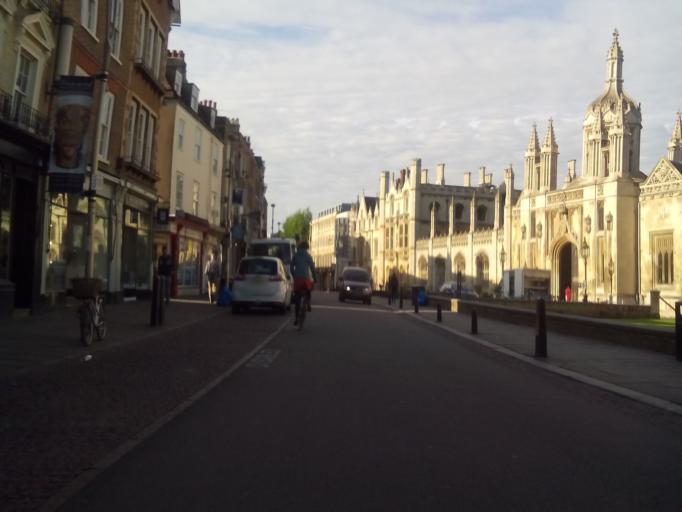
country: GB
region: England
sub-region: Cambridgeshire
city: Cambridge
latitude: 52.2049
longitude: 0.1179
